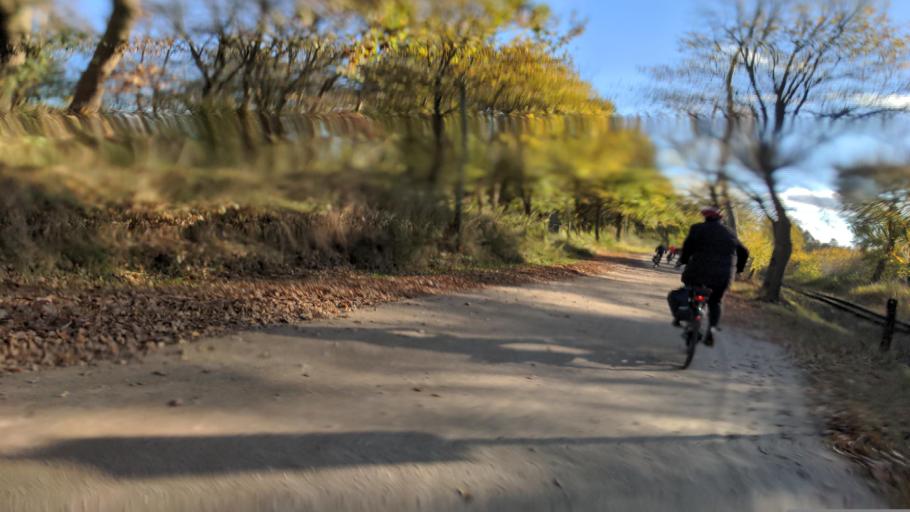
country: DE
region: Schleswig-Holstein
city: Ratekau
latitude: 53.9896
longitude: 10.6967
